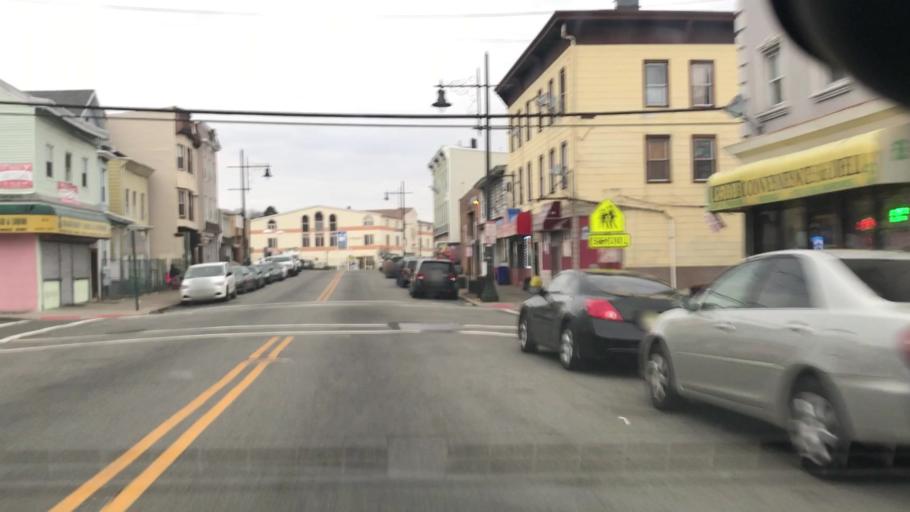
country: US
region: New Jersey
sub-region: Passaic County
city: Paterson
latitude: 40.9046
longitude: -74.1688
